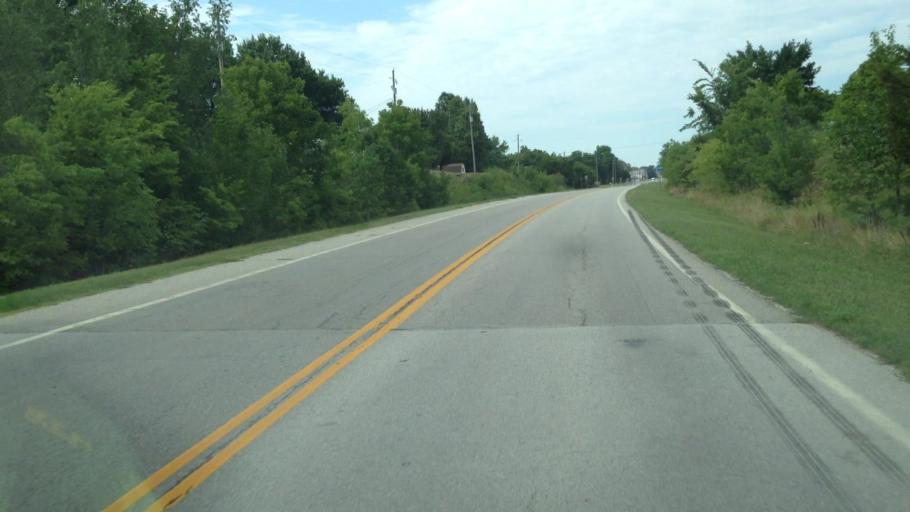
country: US
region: Kansas
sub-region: Labette County
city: Oswego
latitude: 37.1572
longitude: -95.1088
